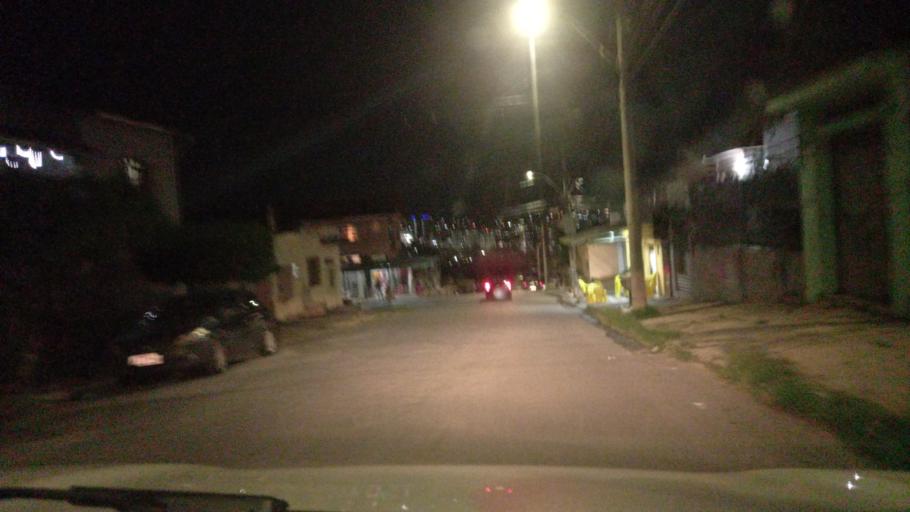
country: BR
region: Minas Gerais
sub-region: Belo Horizonte
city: Belo Horizonte
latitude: -19.8776
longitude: -43.9433
